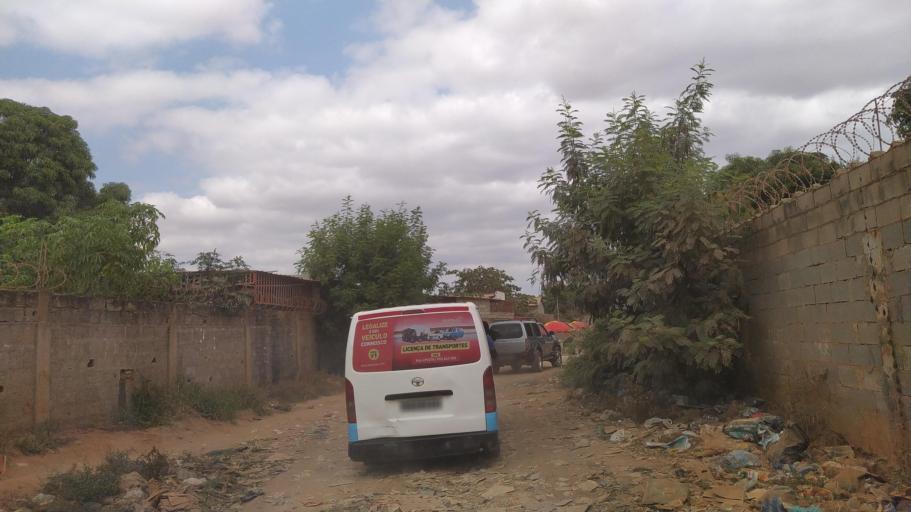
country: AO
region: Luanda
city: Luanda
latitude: -8.9304
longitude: 13.2617
